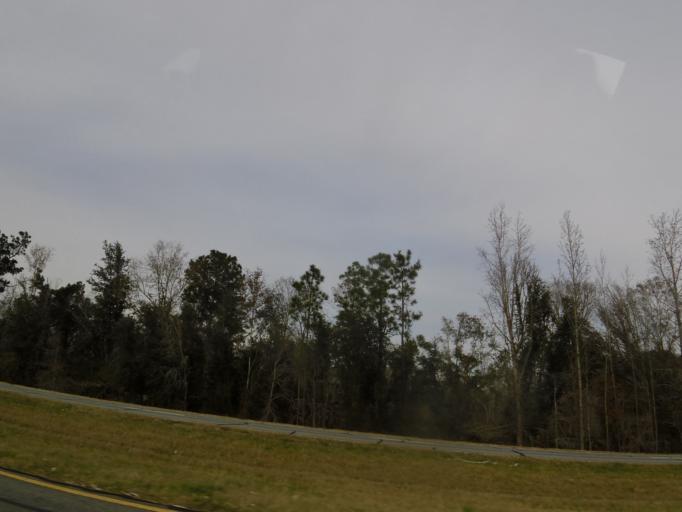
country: US
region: Georgia
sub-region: Seminole County
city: Donalsonville
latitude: 31.0262
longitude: -84.8432
